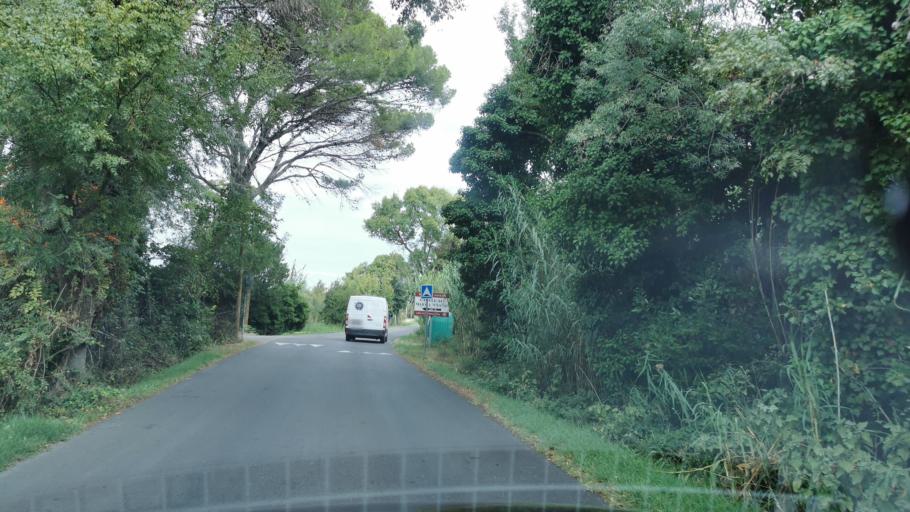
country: FR
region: Languedoc-Roussillon
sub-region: Departement de l'Herault
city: Lespignan
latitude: 43.2271
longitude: 3.1939
